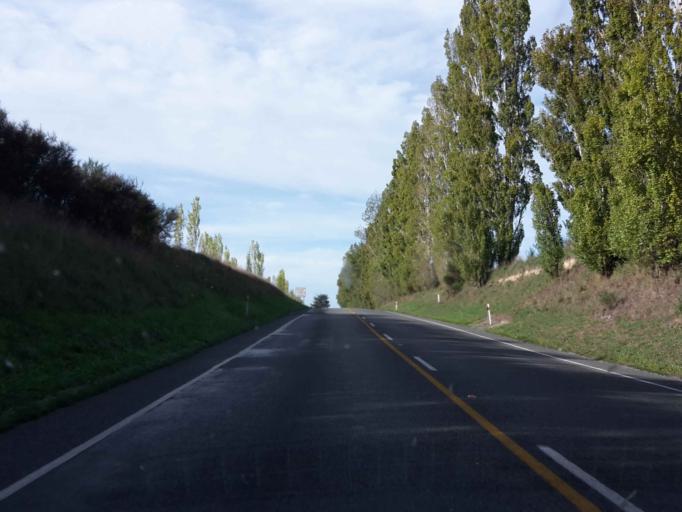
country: NZ
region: Canterbury
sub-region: Ashburton District
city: Tinwald
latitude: -44.0485
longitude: 171.4115
